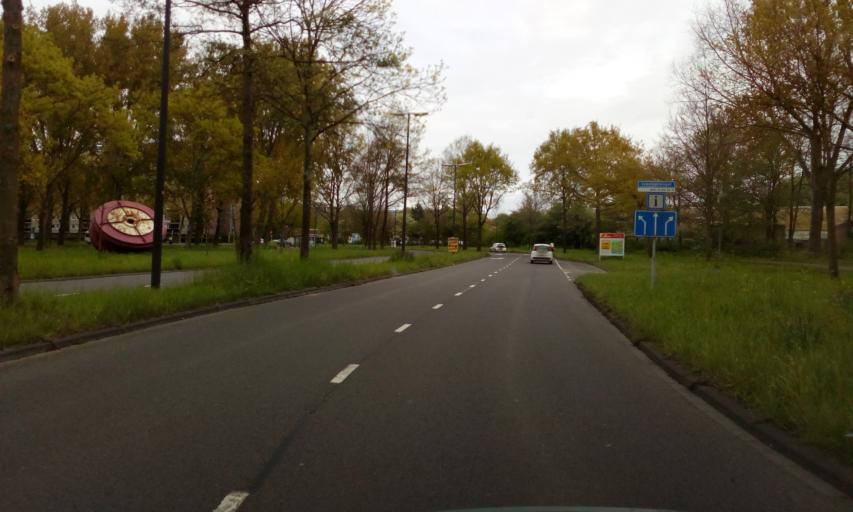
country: NL
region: South Holland
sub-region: Gemeente Vlaardingen
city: Vlaardingen
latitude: 51.9243
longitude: 4.3527
